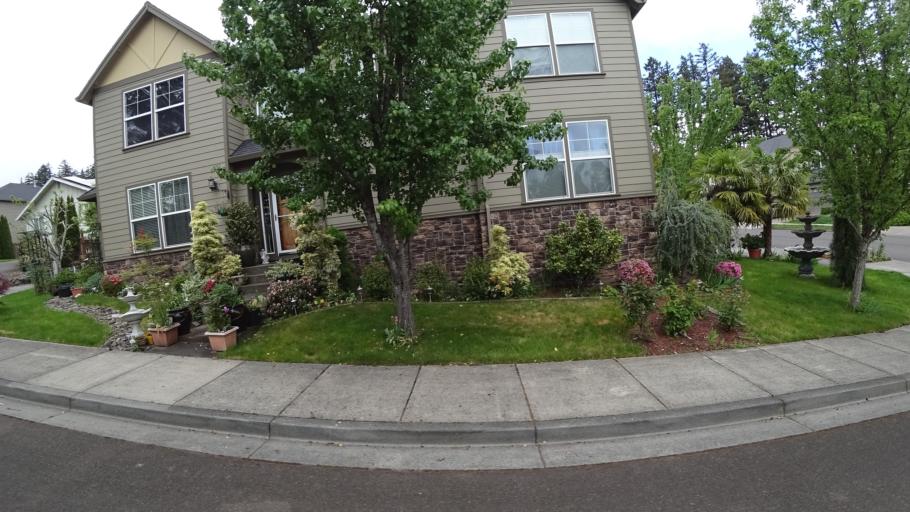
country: US
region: Oregon
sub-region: Washington County
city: Beaverton
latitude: 45.4495
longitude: -122.8353
